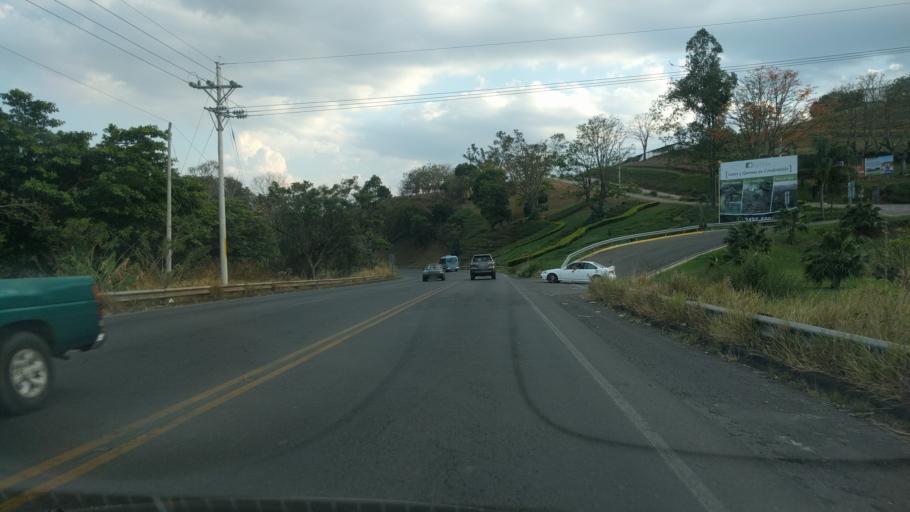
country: CR
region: Alajuela
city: Naranjo
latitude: 10.0722
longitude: -84.3713
